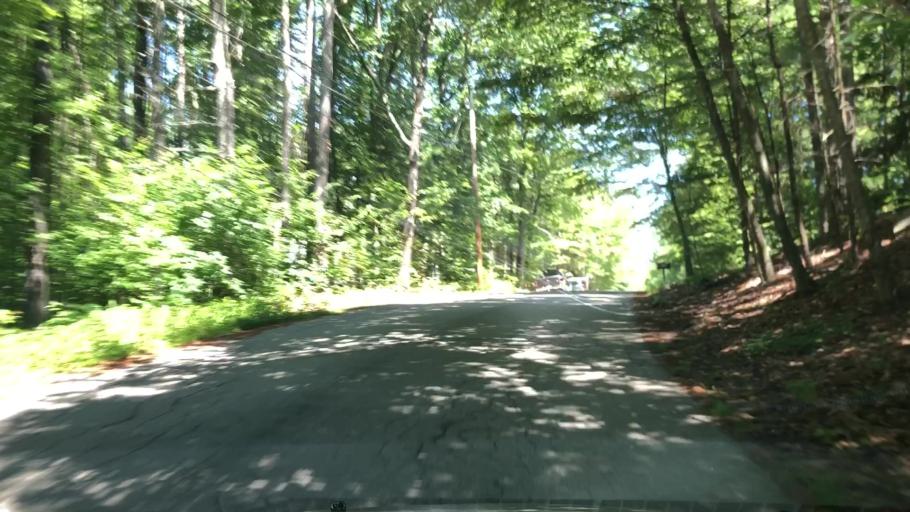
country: US
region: New Hampshire
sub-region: Hillsborough County
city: Milford
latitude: 42.8347
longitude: -71.5866
